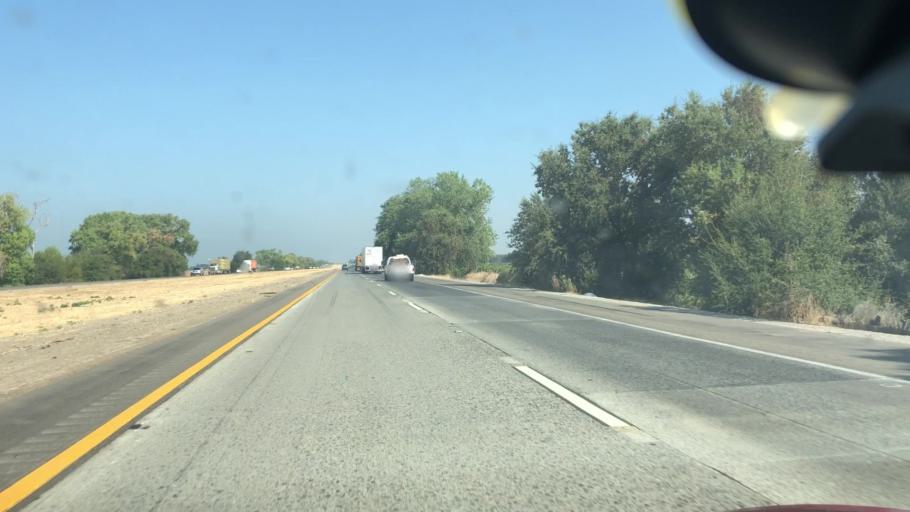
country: US
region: California
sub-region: San Joaquin County
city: Thornton
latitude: 38.2123
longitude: -121.4209
